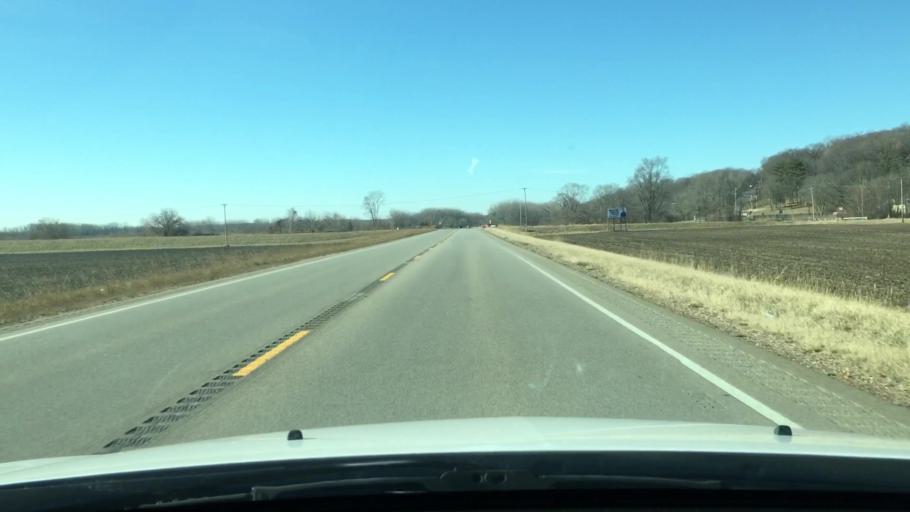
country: US
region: Illinois
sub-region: Peoria County
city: Glasford
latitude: 40.5520
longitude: -89.8009
